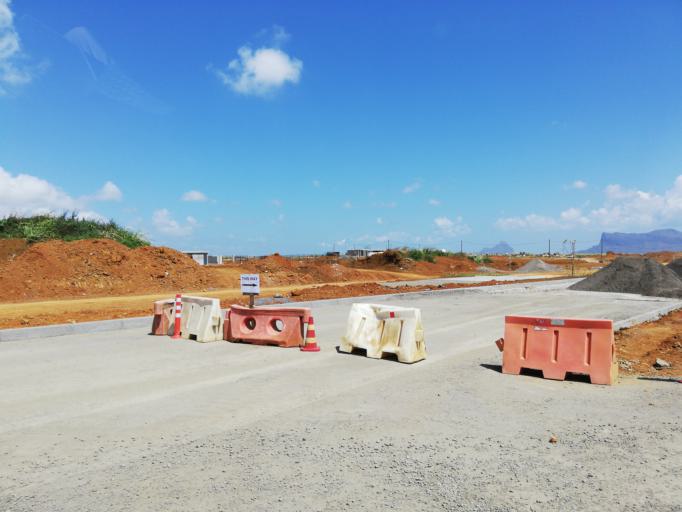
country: MU
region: Moka
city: Saint Pierre
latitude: -20.2278
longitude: 57.5254
